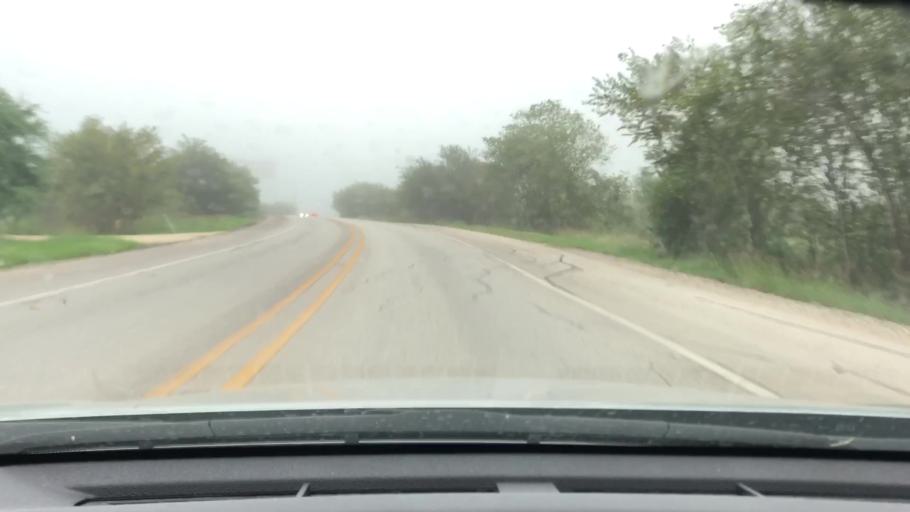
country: US
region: Texas
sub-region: Bexar County
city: Converse
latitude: 29.4742
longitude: -98.3129
